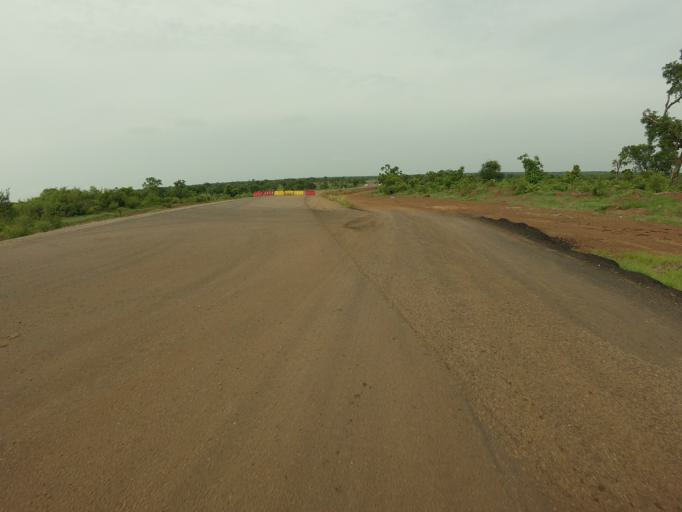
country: GH
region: Northern
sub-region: Yendi
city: Yendi
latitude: 9.7974
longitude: -0.1131
